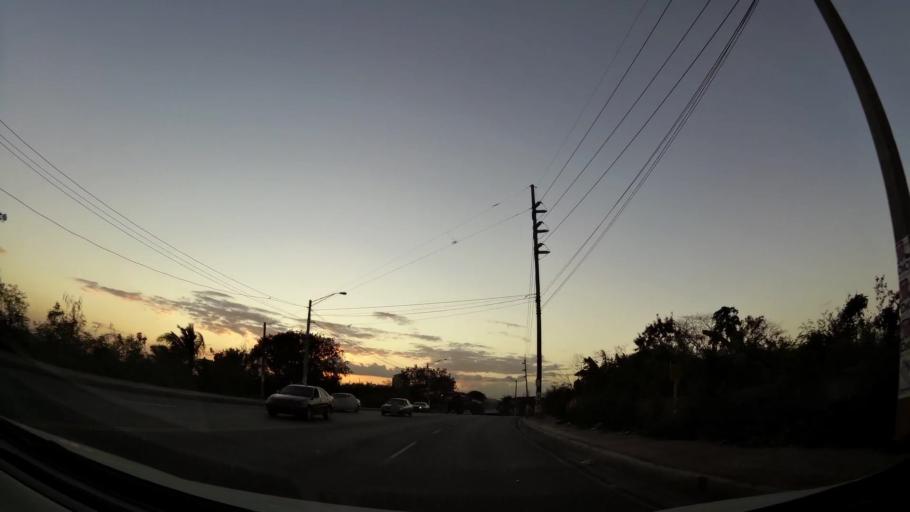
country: DO
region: Santo Domingo
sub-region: Santo Domingo
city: Santo Domingo Este
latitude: 18.4839
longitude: -69.8316
